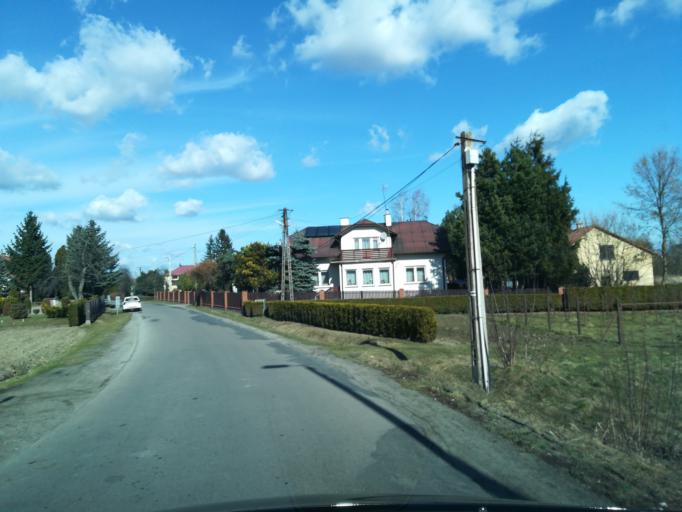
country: PL
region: Subcarpathian Voivodeship
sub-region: Powiat lancucki
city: Kosina
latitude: 50.0836
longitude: 22.3245
